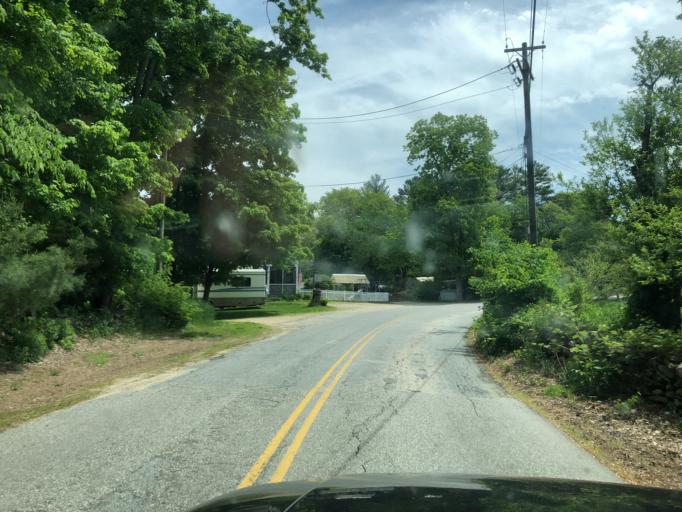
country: US
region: Connecticut
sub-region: Windham County
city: Thompson
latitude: 41.9643
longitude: -71.8250
